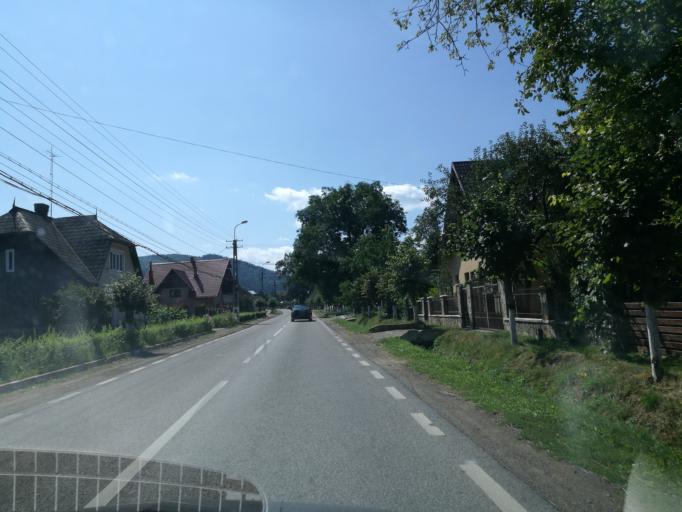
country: RO
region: Suceava
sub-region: Comuna Putna
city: Putna
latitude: 47.8769
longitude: 25.6147
